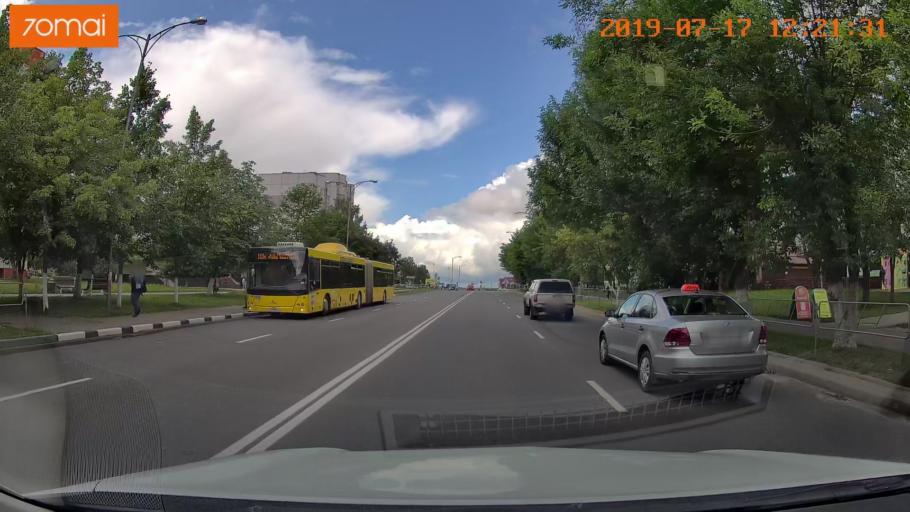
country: BY
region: Minsk
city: Borovlyany
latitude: 54.0048
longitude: 27.6815
